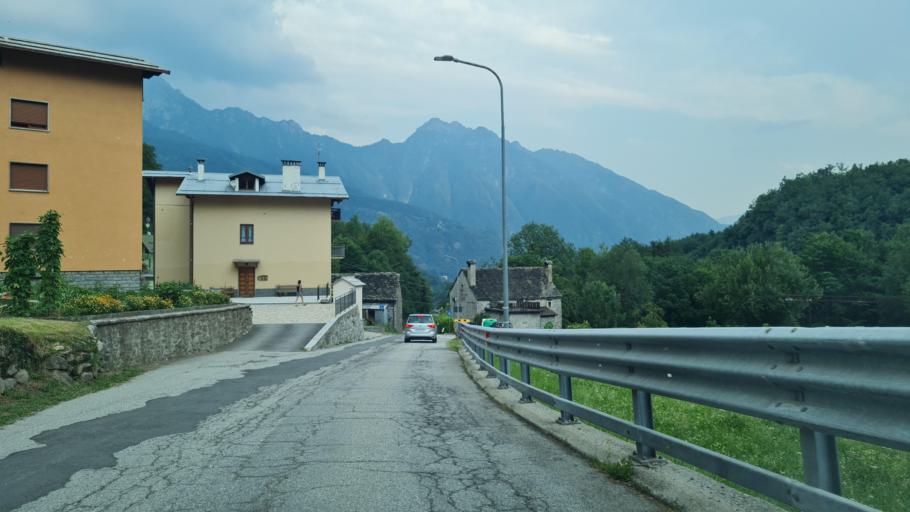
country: IT
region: Piedmont
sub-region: Provincia Verbano-Cusio-Ossola
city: Baceno
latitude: 46.2704
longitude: 8.3081
